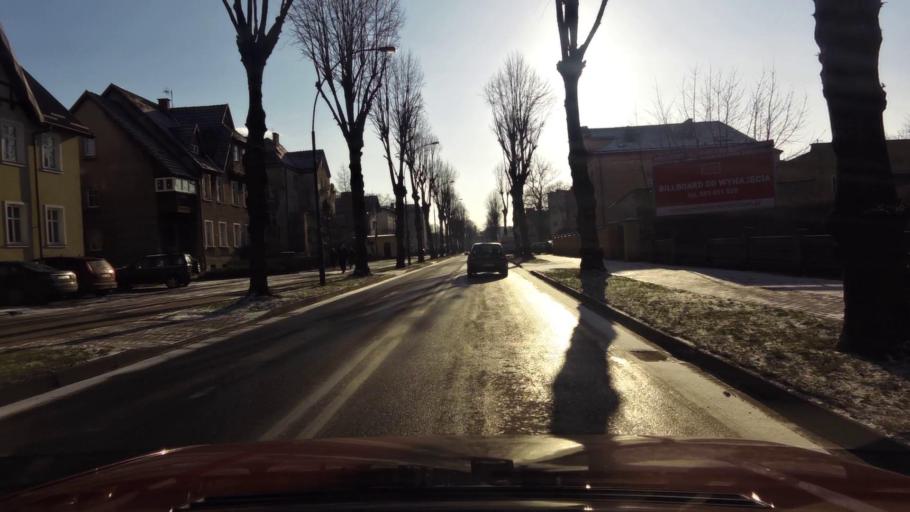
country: PL
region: West Pomeranian Voivodeship
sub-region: Powiat bialogardzki
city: Bialogard
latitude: 54.0099
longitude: 15.9835
